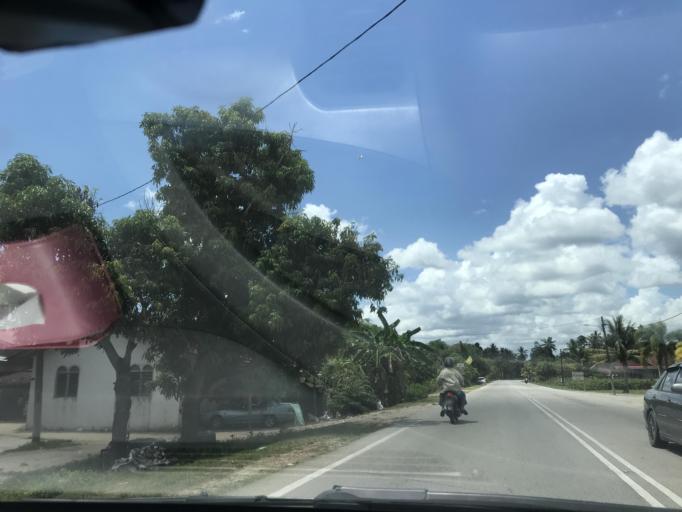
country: MY
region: Kelantan
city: Tumpat
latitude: 6.2055
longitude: 102.1181
